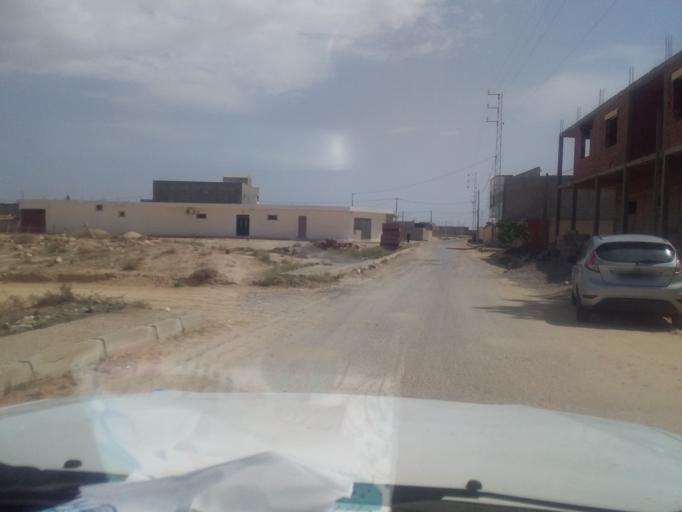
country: TN
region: Madanin
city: Medenine
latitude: 33.5829
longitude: 10.3260
